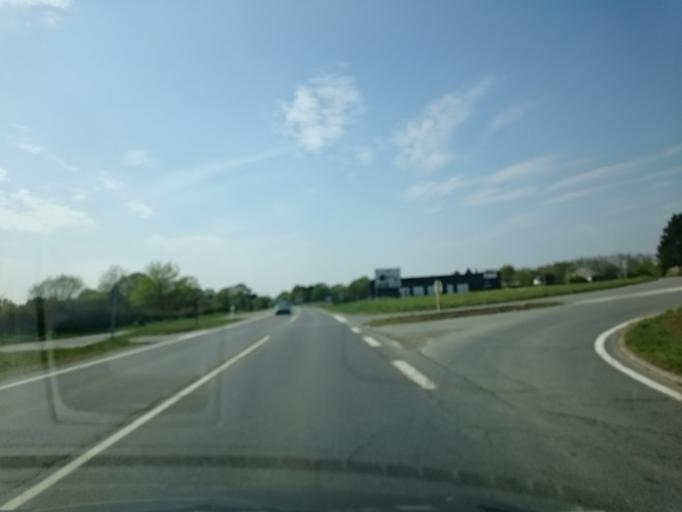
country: FR
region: Brittany
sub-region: Departement d'Ille-et-Vilaine
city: Chantepie
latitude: 48.0790
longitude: -1.5978
